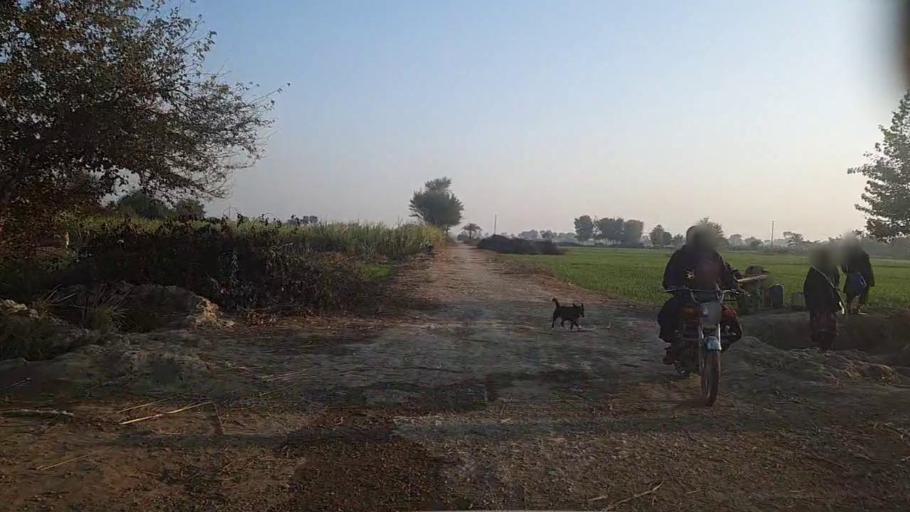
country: PK
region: Sindh
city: Khairpur
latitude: 28.0566
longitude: 69.7584
